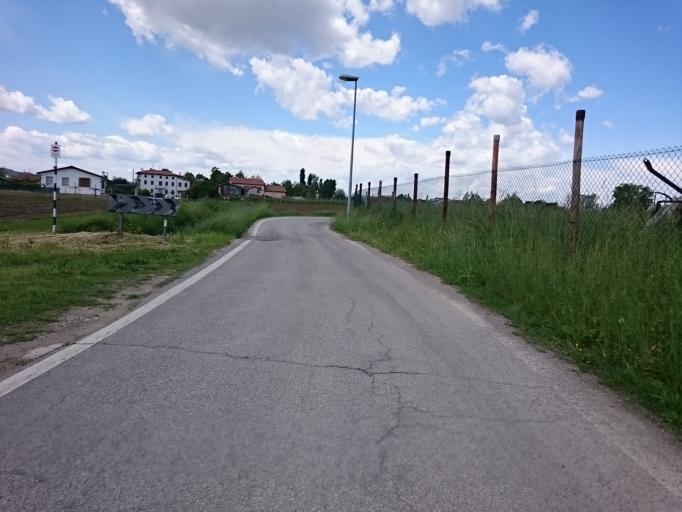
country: IT
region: Veneto
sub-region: Provincia di Padova
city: Montegrotto Terme
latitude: 45.3337
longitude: 11.8038
